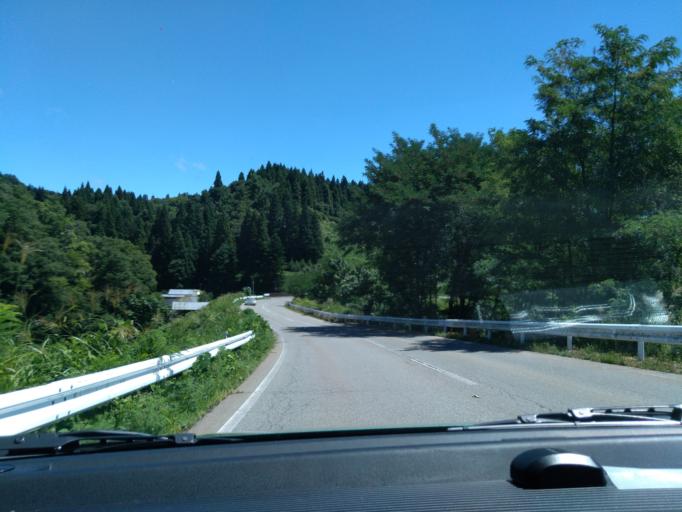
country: JP
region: Akita
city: Yokotemachi
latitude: 39.2487
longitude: 140.5657
